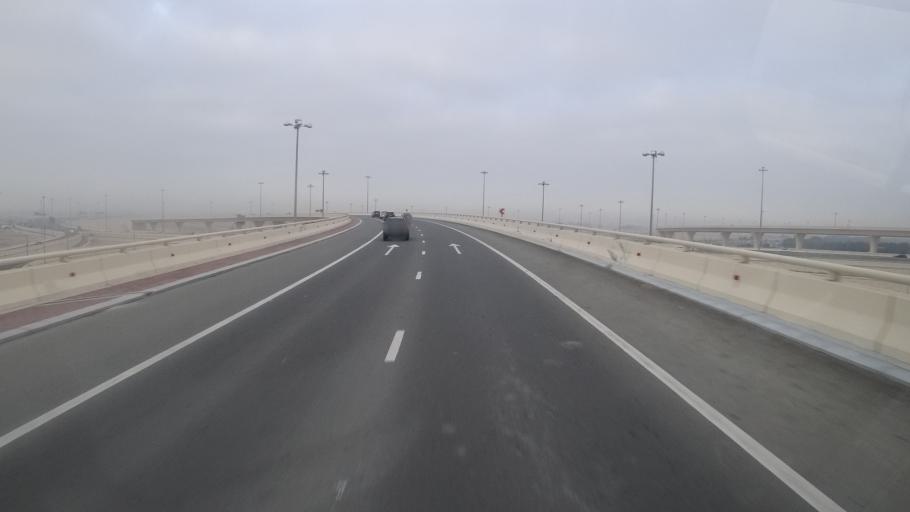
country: AE
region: Abu Dhabi
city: Abu Dhabi
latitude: 24.3082
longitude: 54.6032
